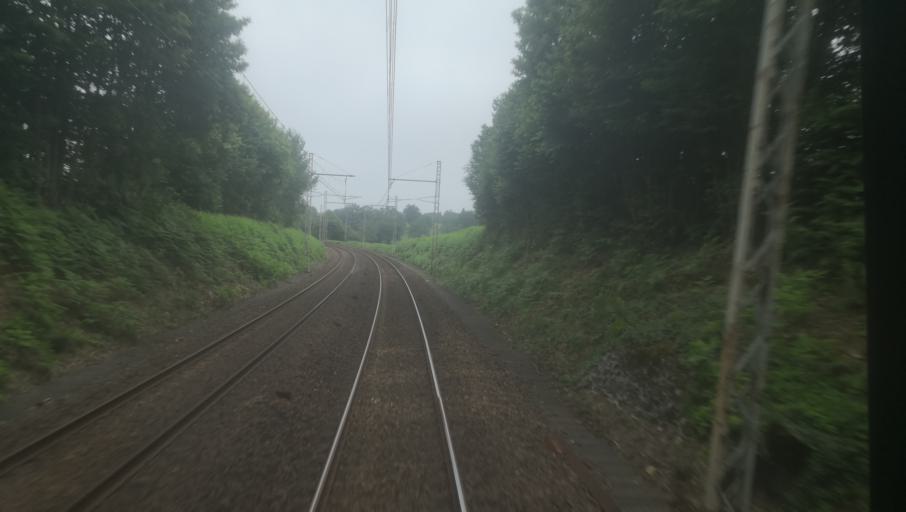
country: FR
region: Limousin
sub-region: Departement de la Creuse
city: Saint-Agnant-de-Versillat
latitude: 46.3351
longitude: 1.5381
